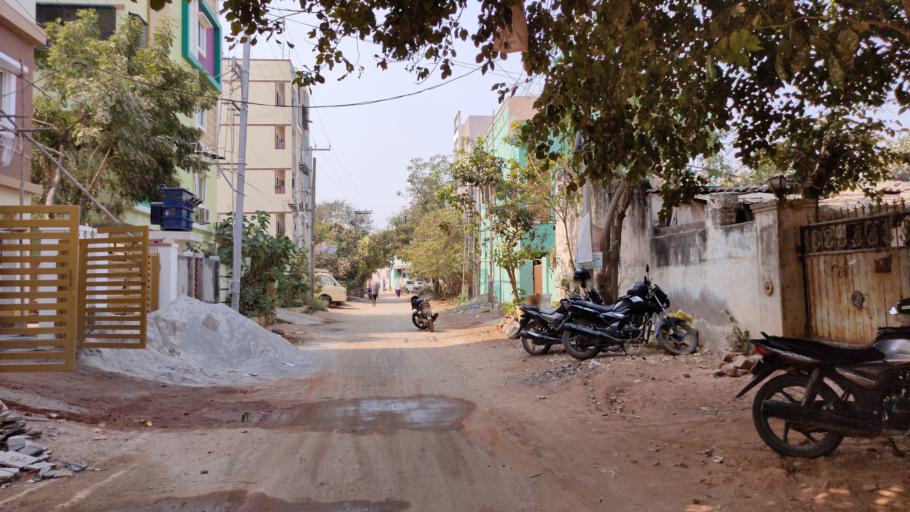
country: IN
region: Telangana
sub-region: Rangareddi
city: Quthbullapur
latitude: 17.4927
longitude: 78.4639
